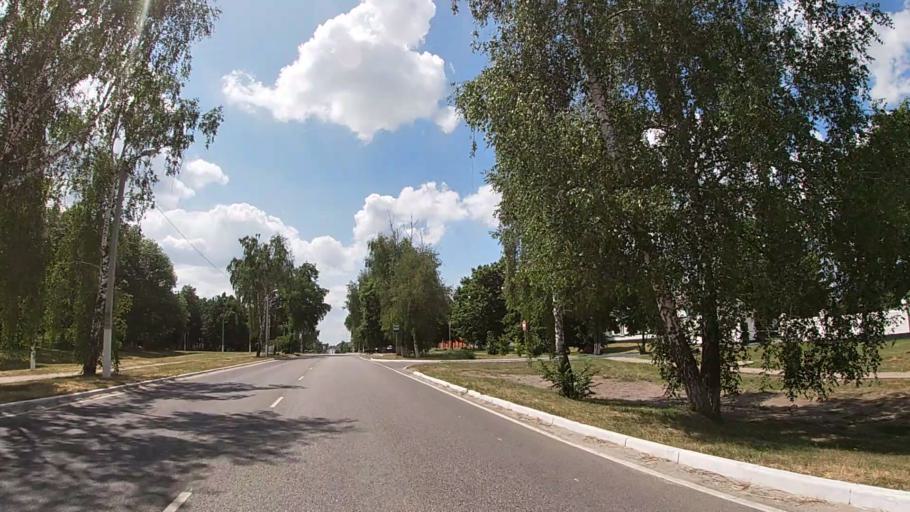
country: RU
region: Belgorod
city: Grayvoron
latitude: 50.4867
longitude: 35.6906
